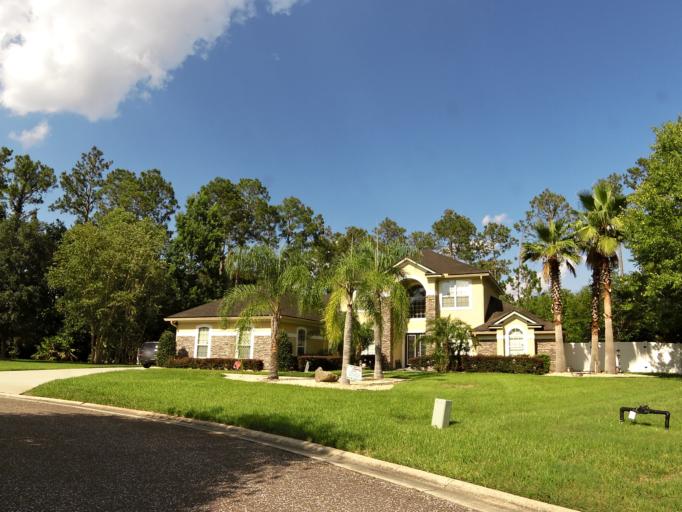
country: US
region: Florida
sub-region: Saint Johns County
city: Fruit Cove
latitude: 30.0649
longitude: -81.6506
